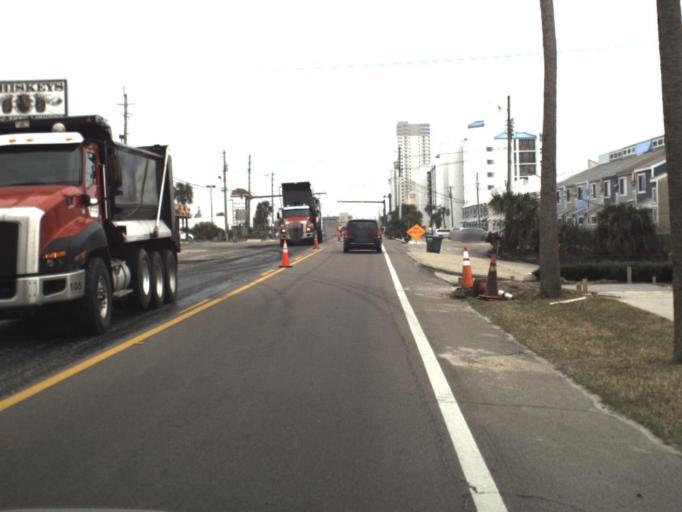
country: US
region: Florida
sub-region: Bay County
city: Laguna Beach
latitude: 30.2247
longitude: -85.8942
